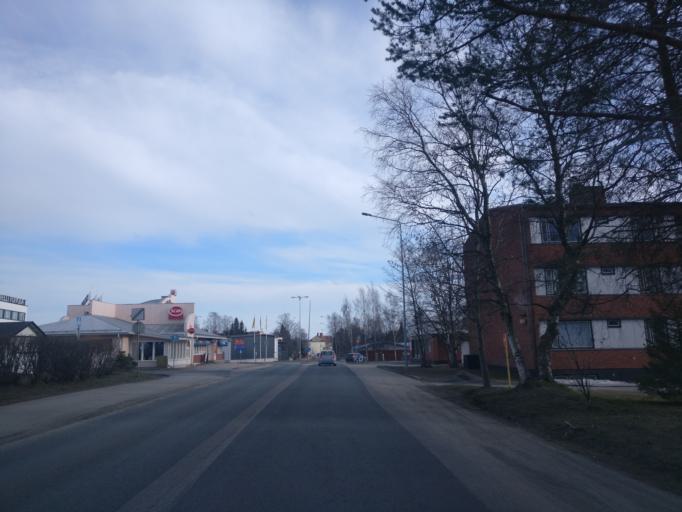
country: FI
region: Lapland
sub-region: Kemi-Tornio
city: Kemi
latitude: 65.7307
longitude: 24.5988
